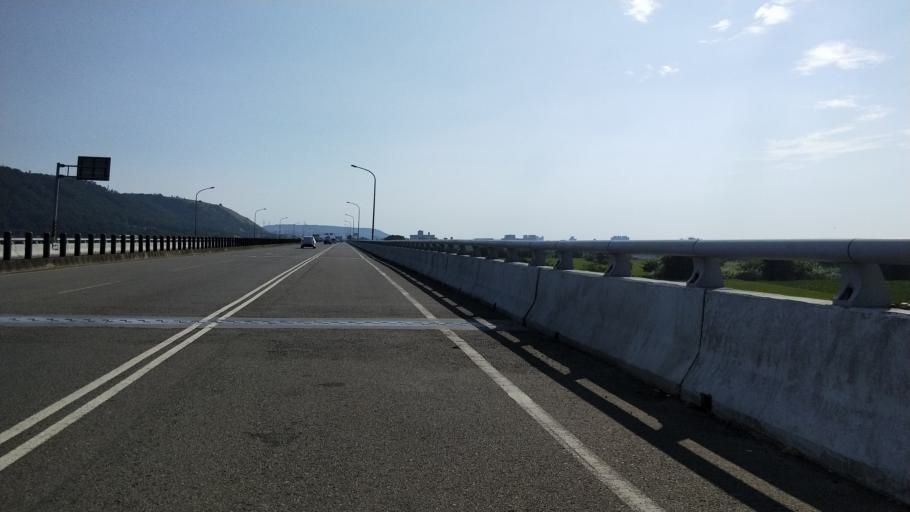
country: TW
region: Taiwan
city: Fengyuan
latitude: 24.3762
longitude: 120.6481
